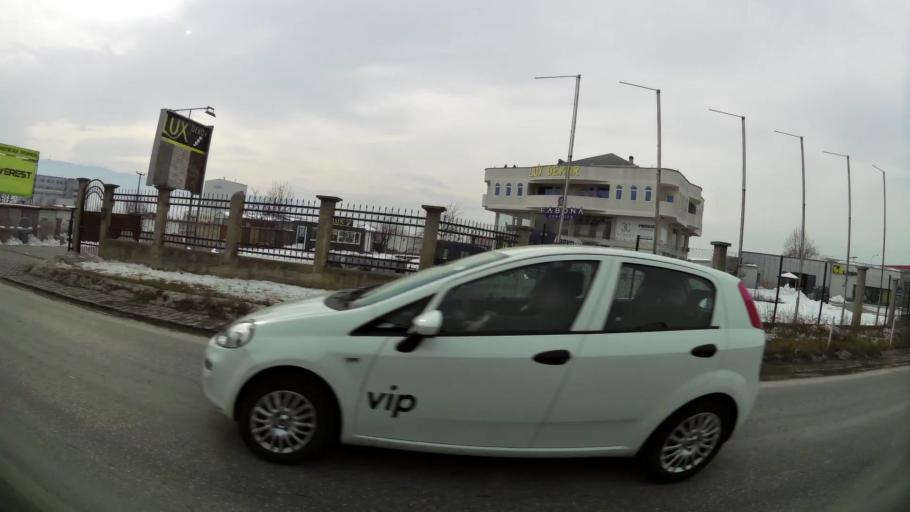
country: MK
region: Suto Orizari
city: Suto Orizare
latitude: 42.0380
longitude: 21.3970
